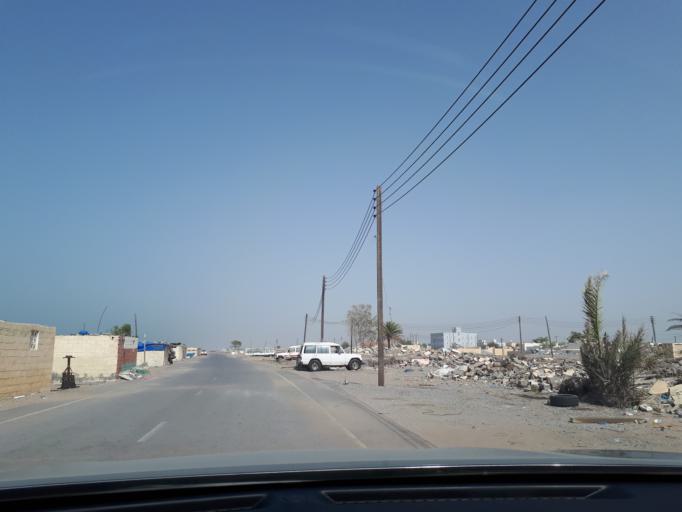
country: OM
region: Al Batinah
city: Barka'
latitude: 23.7088
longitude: 57.9067
